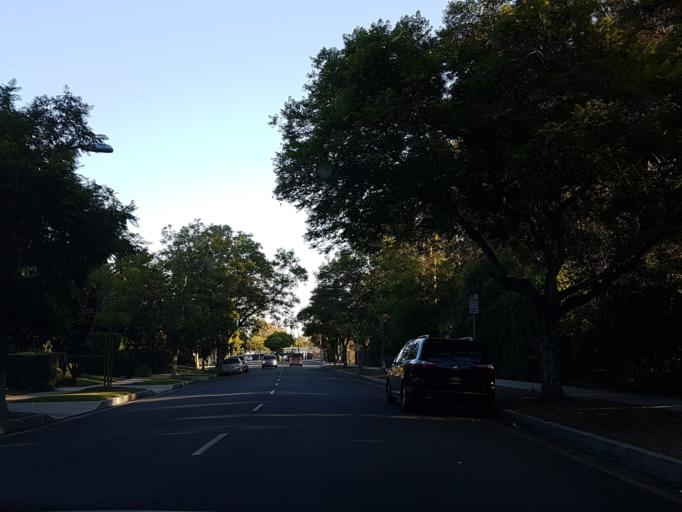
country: US
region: California
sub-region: Los Angeles County
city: Century City
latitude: 34.0704
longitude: -118.4173
